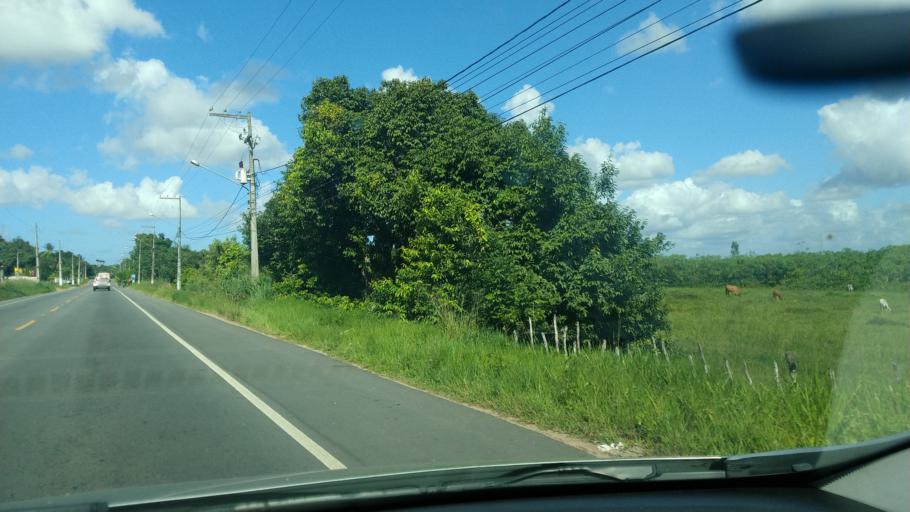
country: BR
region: Rio Grande do Norte
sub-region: Sao Goncalo Do Amarante
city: Sao Goncalo do Amarante
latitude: -5.7886
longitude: -35.3225
